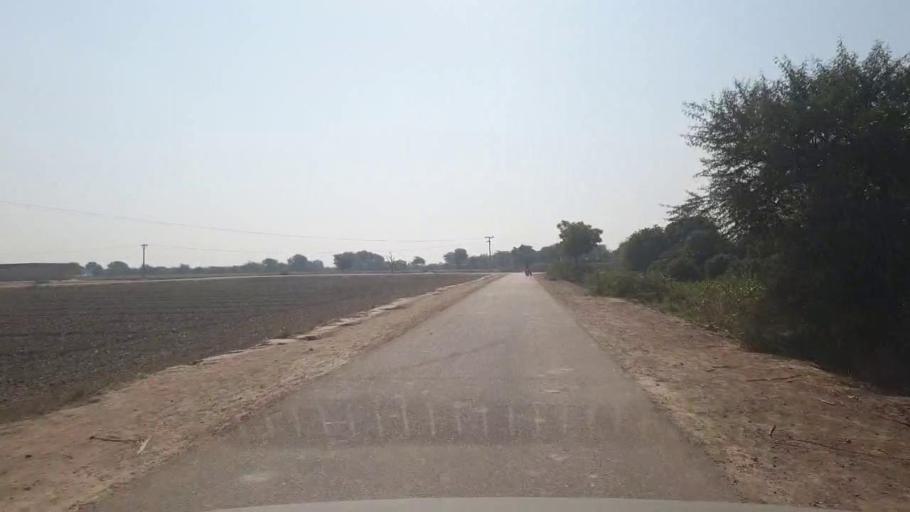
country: PK
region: Sindh
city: Chambar
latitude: 25.2476
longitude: 68.8295
